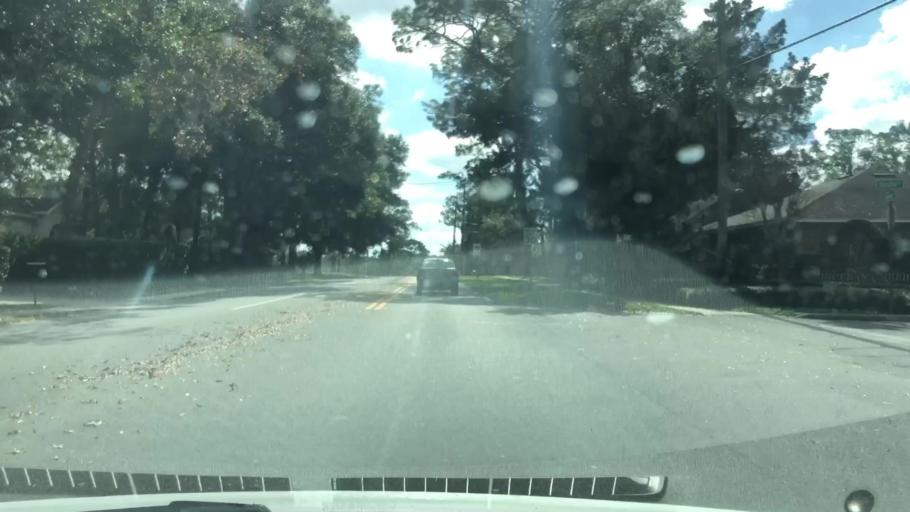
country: US
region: Florida
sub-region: Seminole County
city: Altamonte Springs
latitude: 28.6901
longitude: -81.3862
